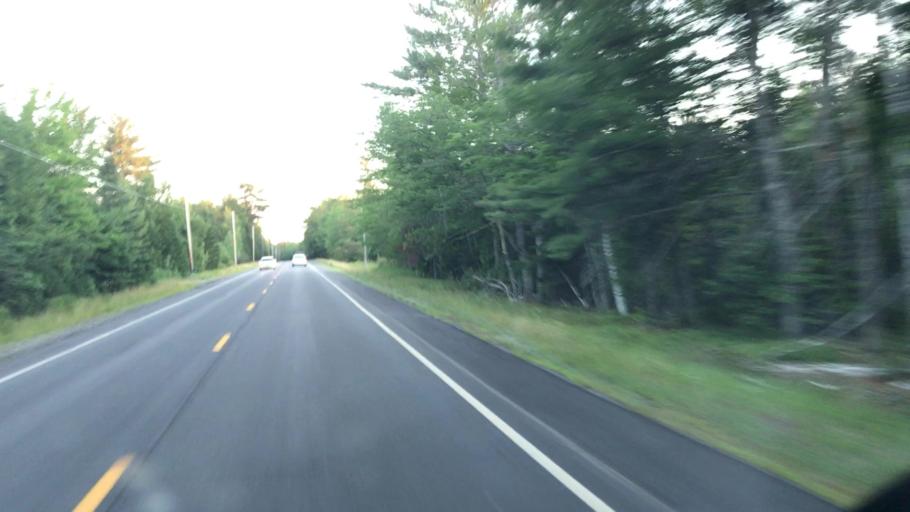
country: US
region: Maine
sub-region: Penobscot County
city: Medway
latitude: 45.5821
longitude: -68.3171
